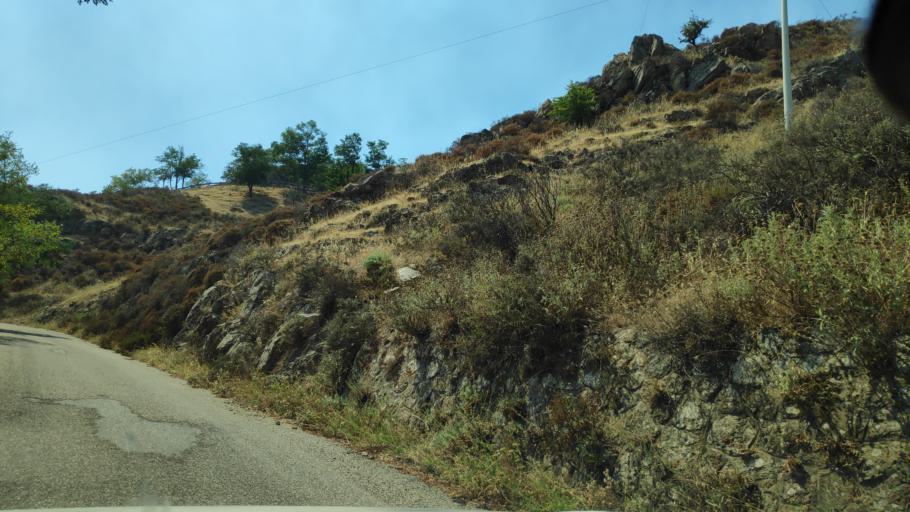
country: IT
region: Calabria
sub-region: Provincia di Reggio Calabria
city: Bova
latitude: 38.0046
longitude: 15.9311
